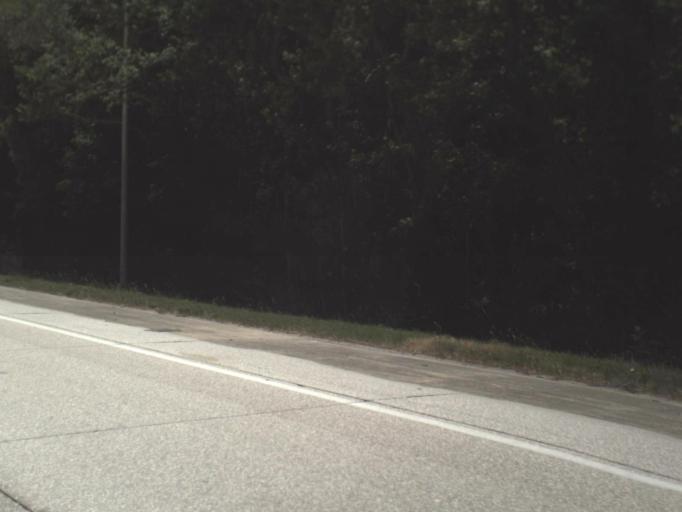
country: US
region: Florida
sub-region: Saint Johns County
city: Fruit Cove
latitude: 30.2256
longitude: -81.5745
